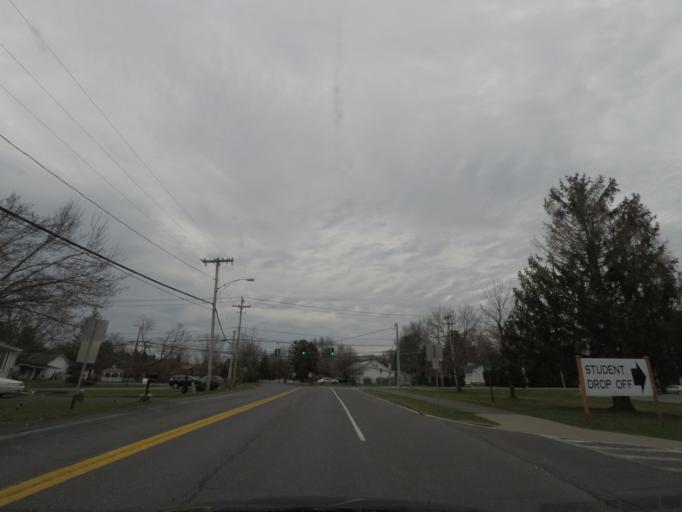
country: US
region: New York
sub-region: Albany County
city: Delmar
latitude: 42.6123
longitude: -73.8587
